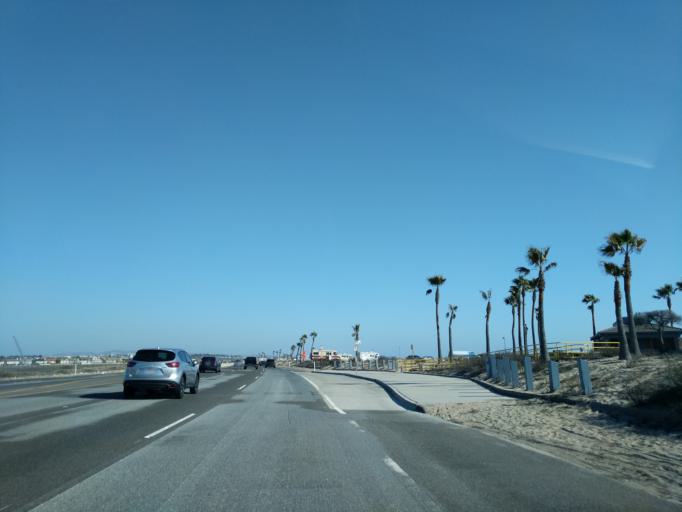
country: US
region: California
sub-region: Orange County
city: Huntington Beach
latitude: 33.6393
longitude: -117.9728
